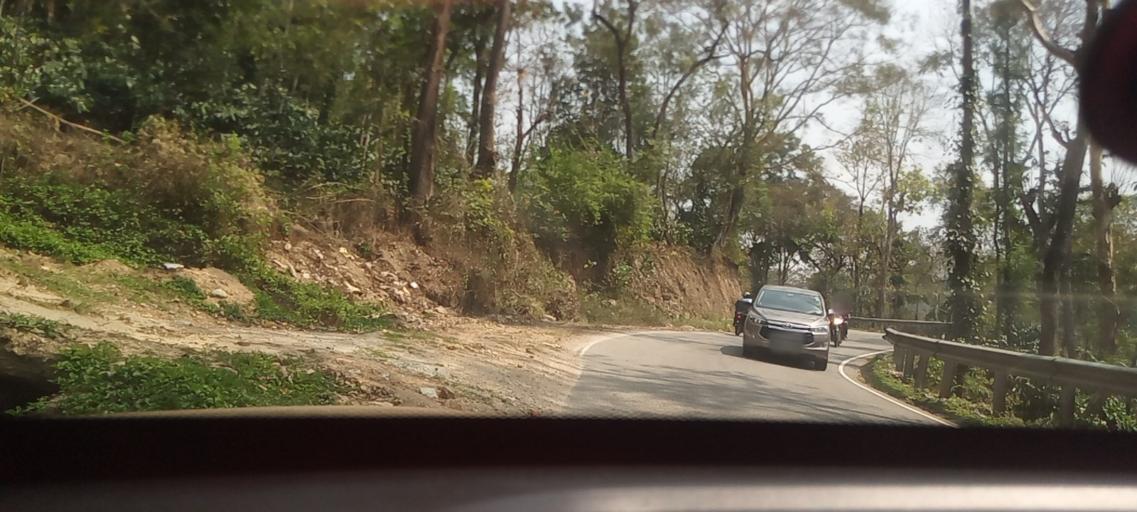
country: IN
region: Karnataka
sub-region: Chikmagalur
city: Mudigere
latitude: 13.2744
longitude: 75.6101
